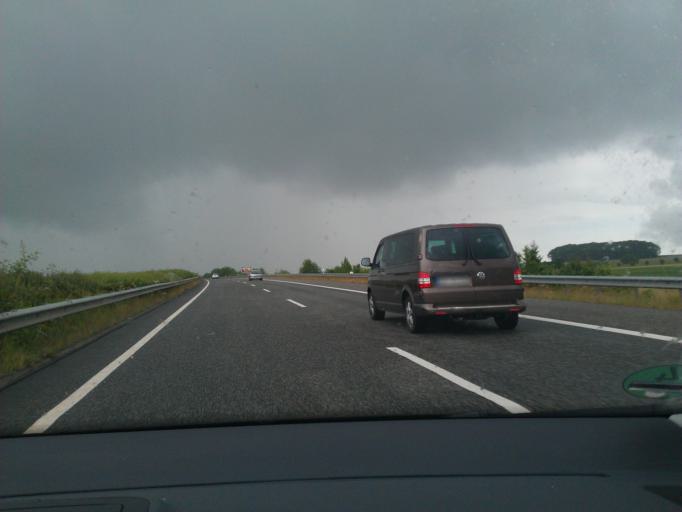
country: DE
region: Rheinland-Pfalz
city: Gindorf
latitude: 50.0211
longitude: 6.6463
